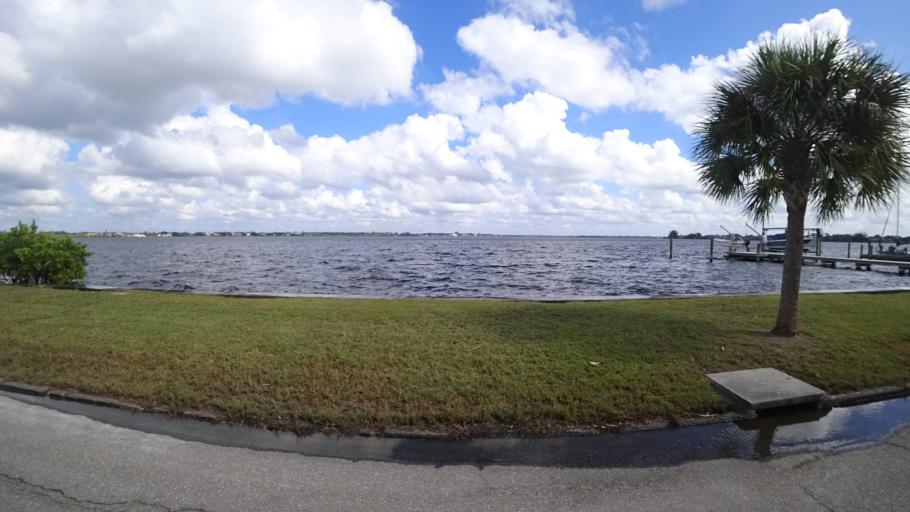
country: US
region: Florida
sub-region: Manatee County
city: Ellenton
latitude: 27.5031
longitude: -82.5325
